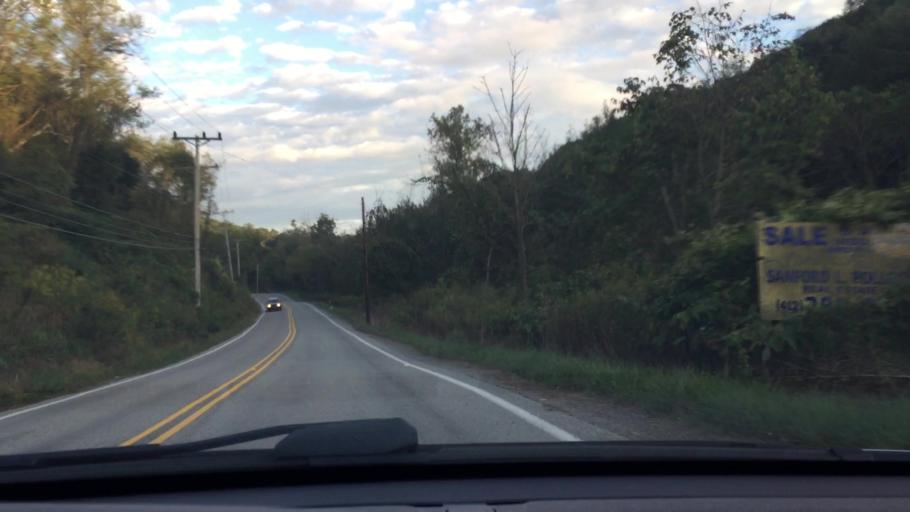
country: US
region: Pennsylvania
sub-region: Westmoreland County
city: Murrysville
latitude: 40.4513
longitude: -79.7273
